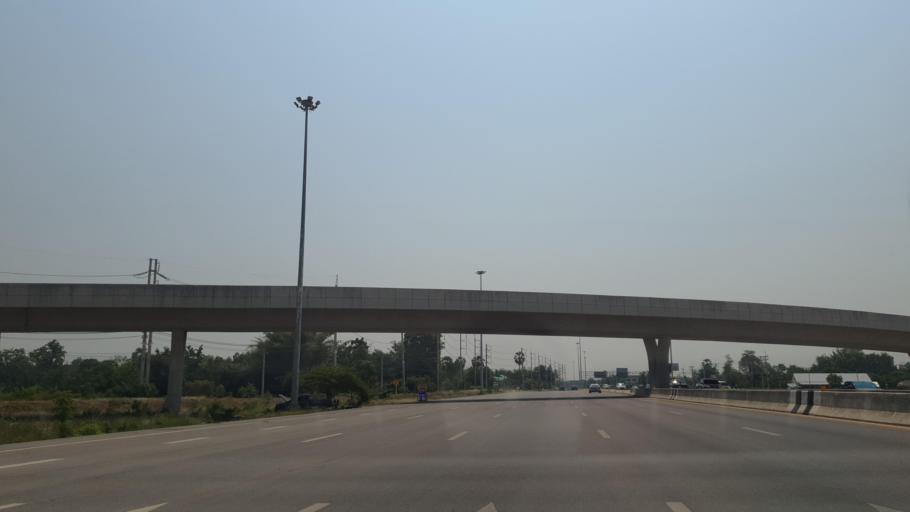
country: TH
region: Kanchanaburi
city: Kanchanaburi
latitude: 14.0437
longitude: 99.6032
